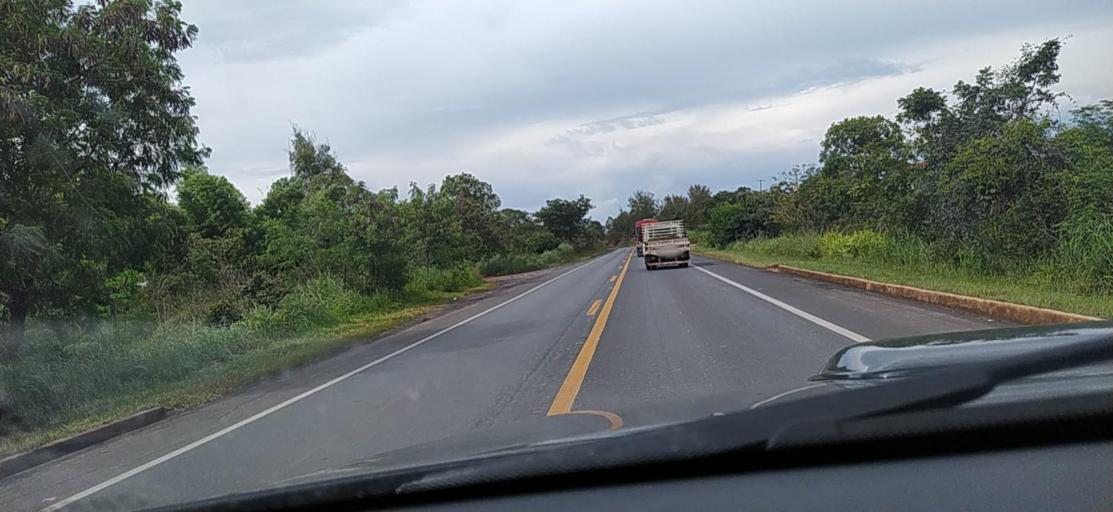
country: BR
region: Minas Gerais
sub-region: Montes Claros
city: Montes Claros
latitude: -16.8415
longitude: -43.8498
